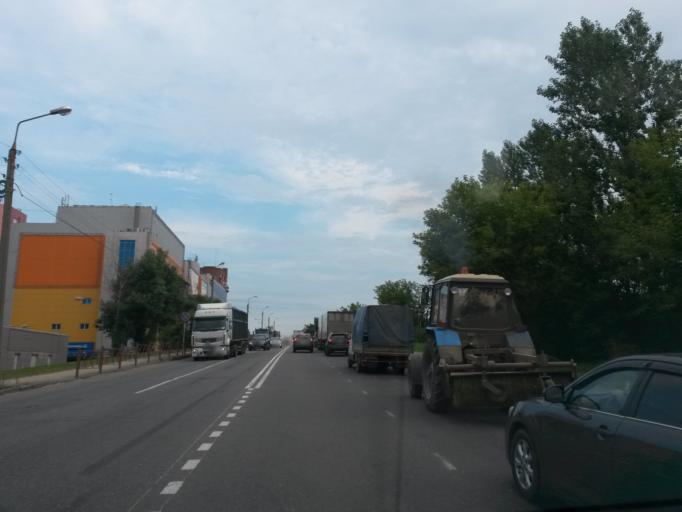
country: RU
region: Jaroslavl
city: Yaroslavl
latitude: 57.5773
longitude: 39.8401
